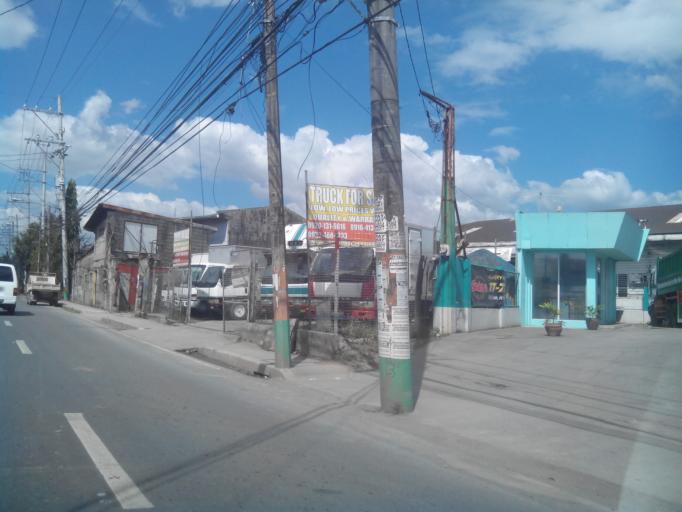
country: PH
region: Calabarzon
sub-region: Province of Rizal
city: Taytay
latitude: 14.5477
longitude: 121.1417
